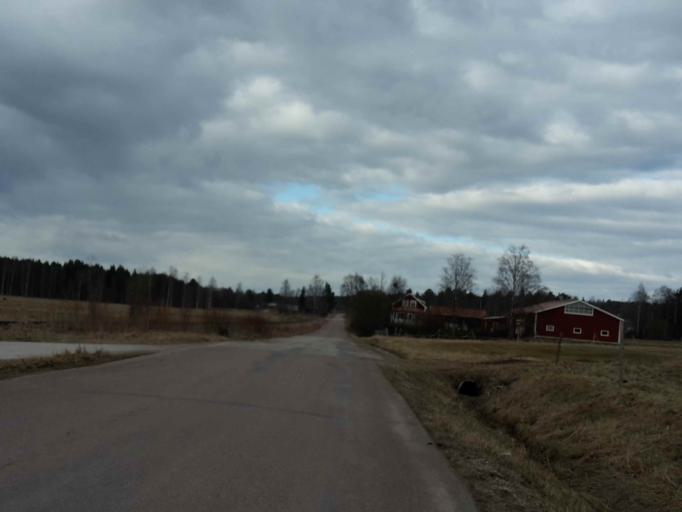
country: SE
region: Dalarna
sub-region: Orsa Kommun
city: Orsa
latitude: 61.1003
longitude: 14.6241
